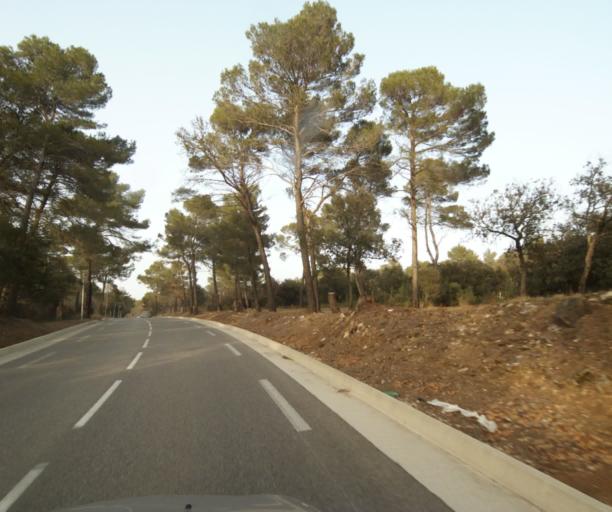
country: FR
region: Provence-Alpes-Cote d'Azur
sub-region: Departement des Bouches-du-Rhone
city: Rognes
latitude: 43.6334
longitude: 5.3602
